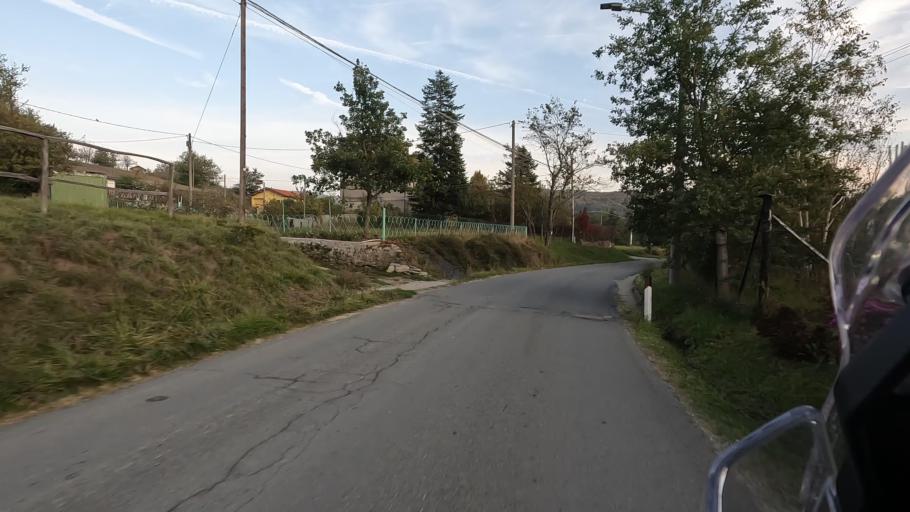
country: IT
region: Liguria
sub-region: Provincia di Savona
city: Mioglia
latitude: 44.4727
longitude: 8.4161
